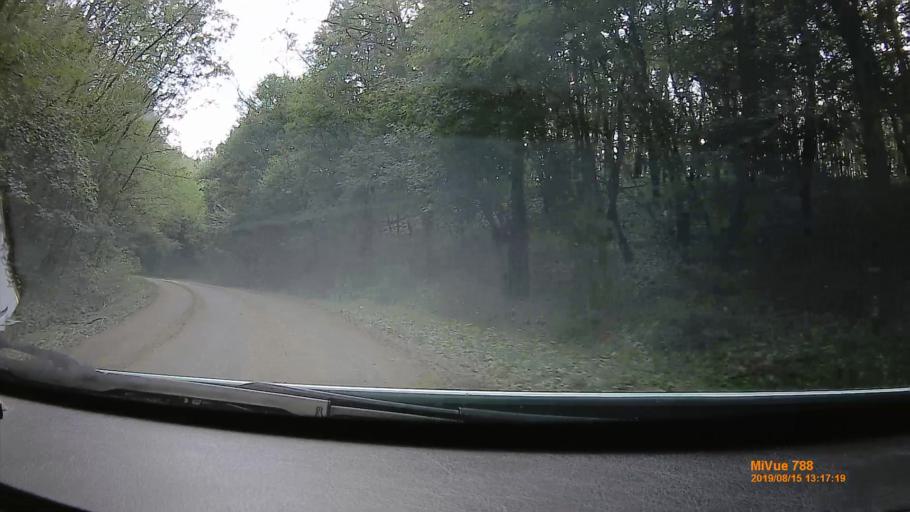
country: HU
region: Borsod-Abauj-Zemplen
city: Sajobabony
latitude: 48.1598
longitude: 20.6553
